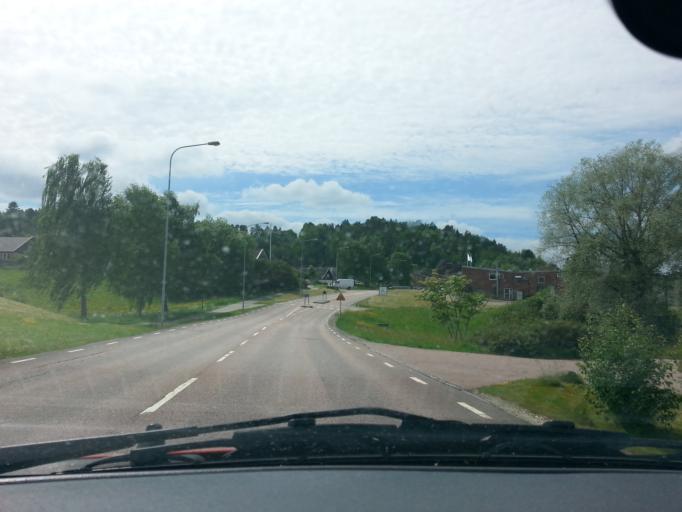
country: SE
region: Vaestra Goetaland
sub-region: Partille Kommun
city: Furulund
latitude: 57.7397
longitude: 12.1376
